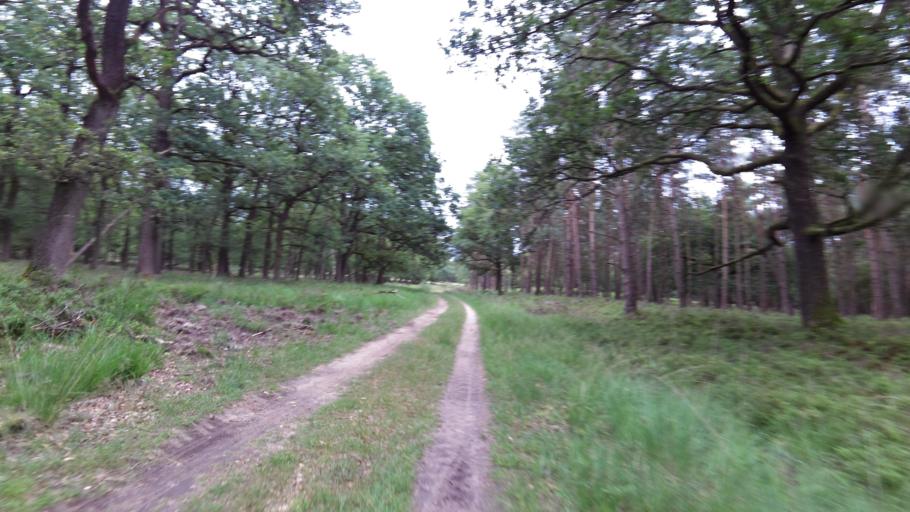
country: NL
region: Gelderland
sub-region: Gemeente Apeldoorn
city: Uddel
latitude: 52.2310
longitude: 5.8275
